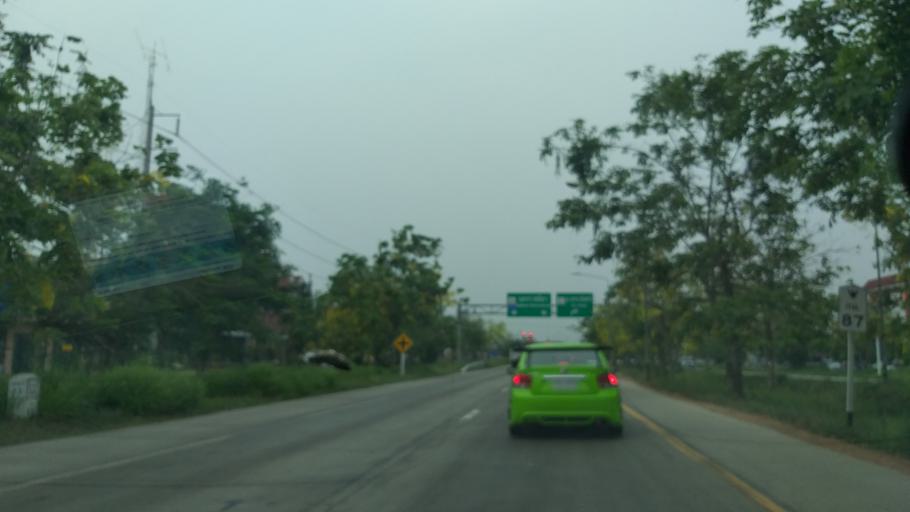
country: TH
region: Chon Buri
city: Ko Chan
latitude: 13.3860
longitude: 101.2787
